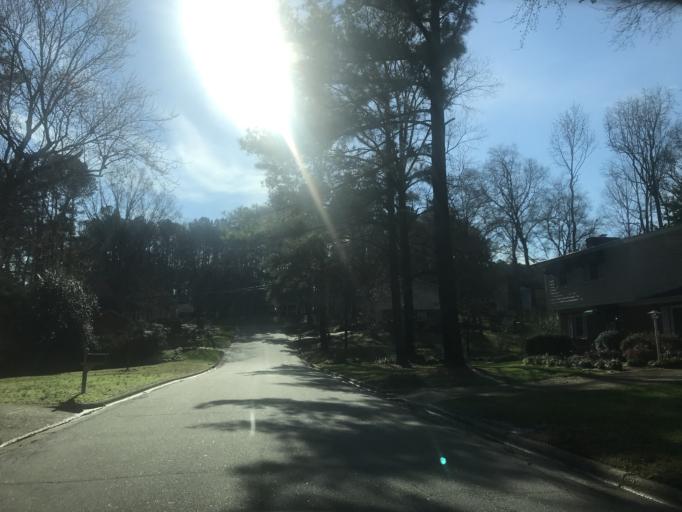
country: US
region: North Carolina
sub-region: Wake County
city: Raleigh
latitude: 35.7491
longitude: -78.6159
